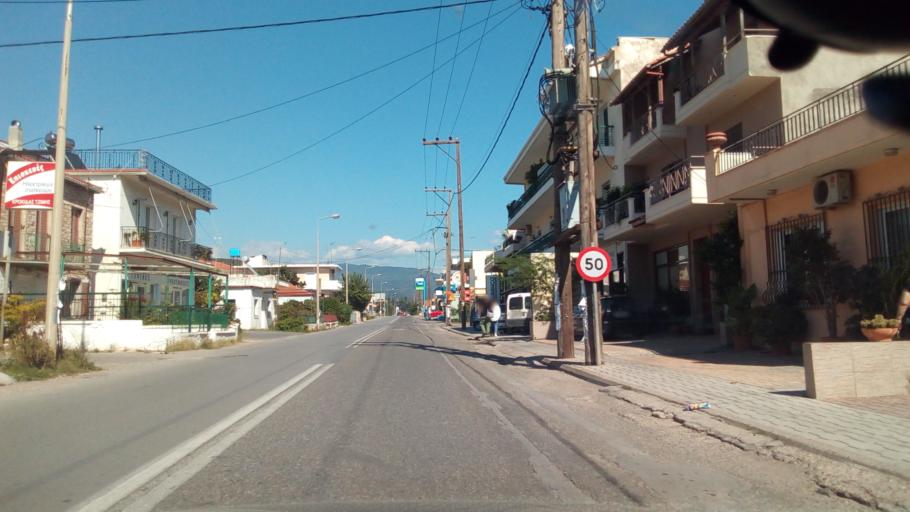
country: GR
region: West Greece
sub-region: Nomos Aitolias kai Akarnanias
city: Nafpaktos
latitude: 38.3965
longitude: 21.8450
